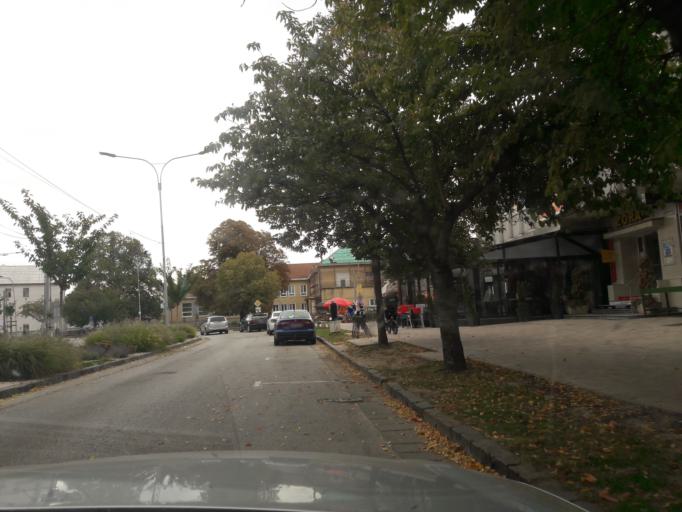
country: SK
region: Nitriansky
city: Surany
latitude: 48.0875
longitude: 18.1855
